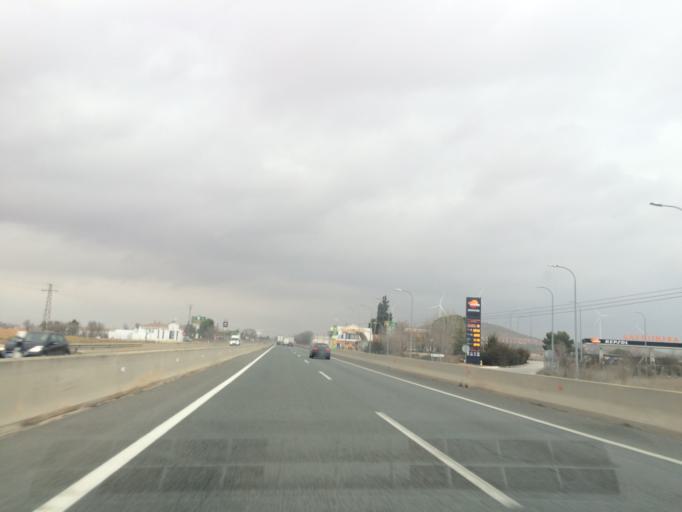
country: ES
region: Castille-La Mancha
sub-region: Province of Toledo
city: Madridejos
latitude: 39.5153
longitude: -3.5243
